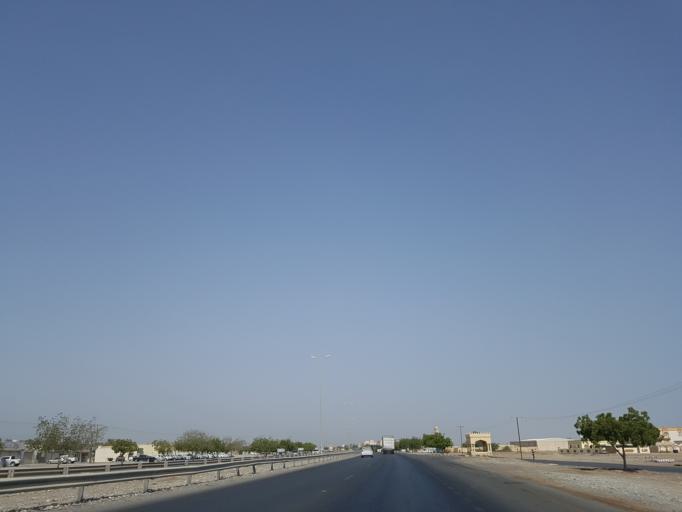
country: OM
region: Al Batinah
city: As Suwayq
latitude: 23.7547
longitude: 57.6065
